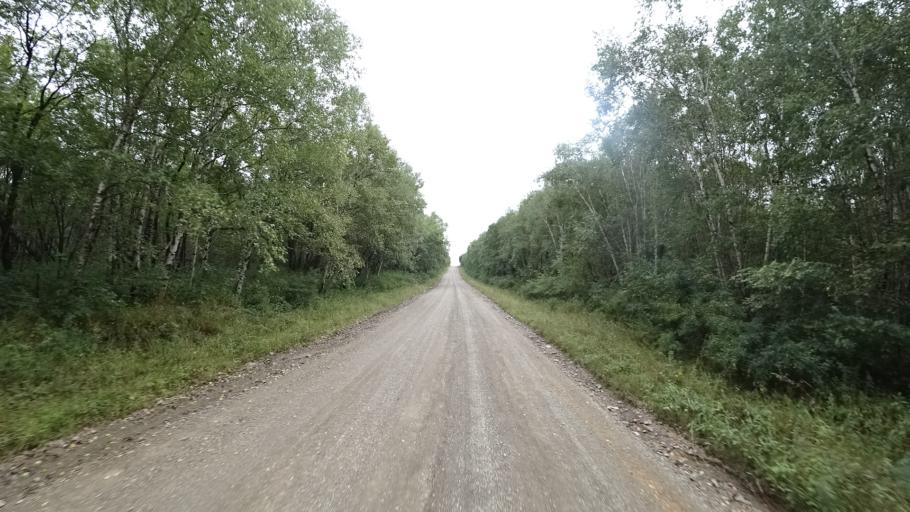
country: RU
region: Primorskiy
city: Ivanovka
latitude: 44.0390
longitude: 132.4971
